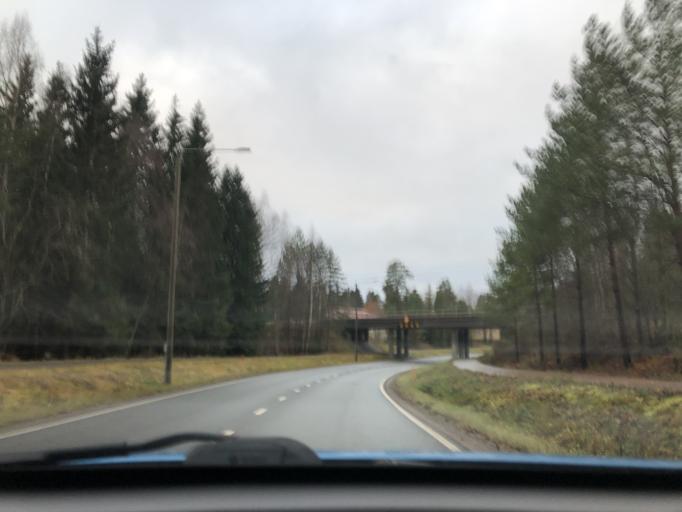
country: FI
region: Pirkanmaa
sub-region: Tampere
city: Kangasala
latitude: 61.5280
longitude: 24.0141
